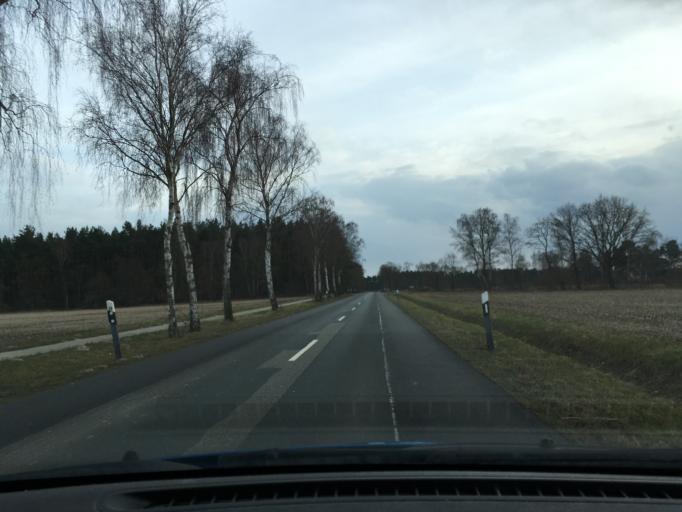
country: DE
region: Lower Saxony
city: Vogelsen
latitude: 53.2683
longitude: 10.3426
